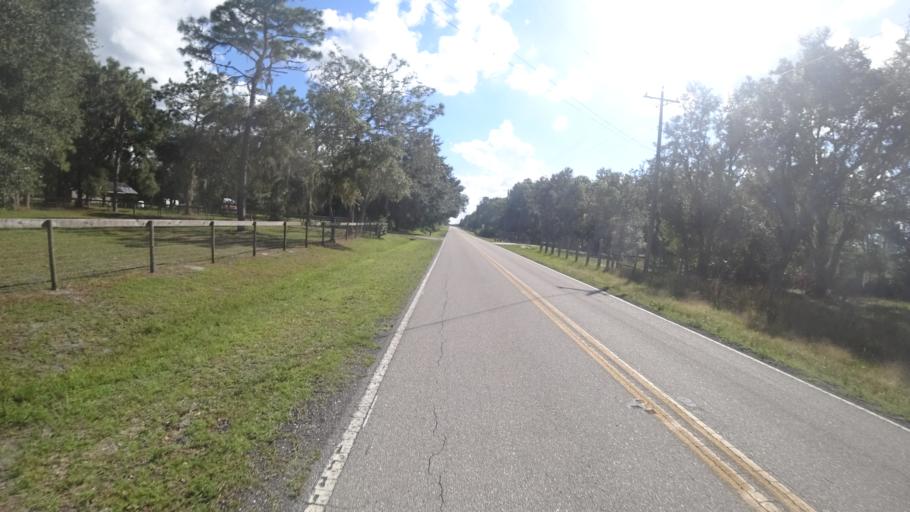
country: US
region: Florida
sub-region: Hillsborough County
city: Wimauma
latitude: 27.4281
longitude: -82.1330
